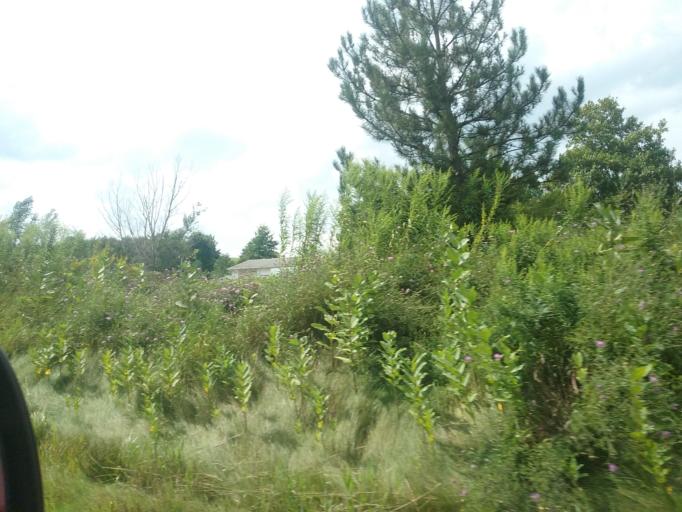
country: US
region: Pennsylvania
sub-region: Tioga County
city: Wellsboro
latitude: 41.7686
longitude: -77.1912
